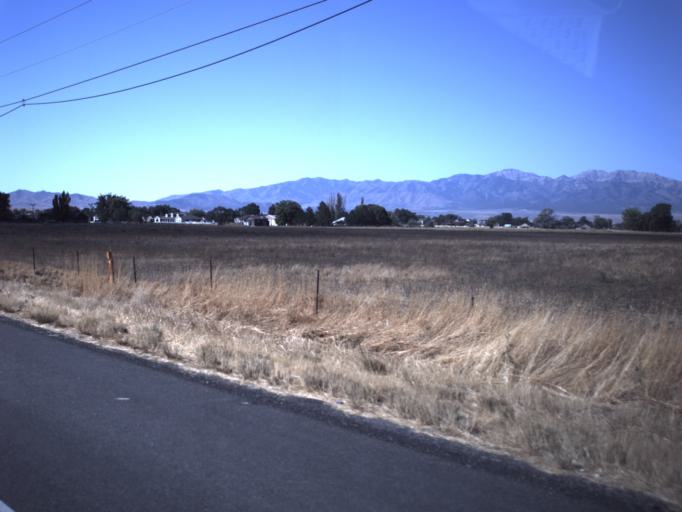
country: US
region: Utah
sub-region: Tooele County
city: Erda
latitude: 40.6197
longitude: -112.2941
